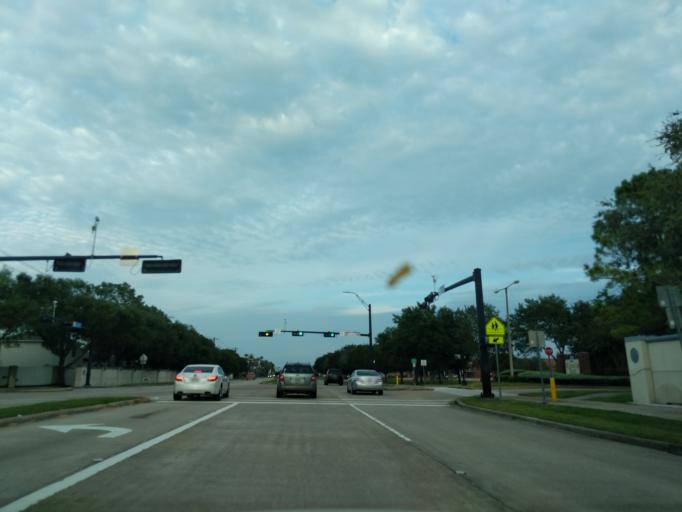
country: US
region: Texas
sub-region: Galveston County
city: Clear Lake Shores
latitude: 29.5271
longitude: -95.0433
